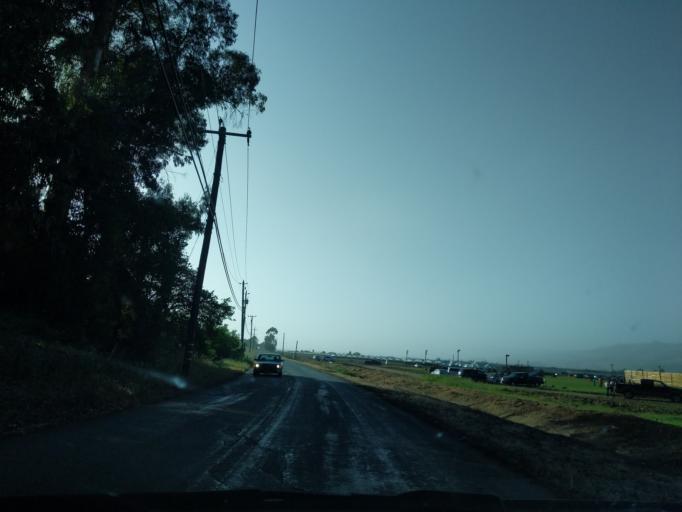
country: US
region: California
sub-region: San Benito County
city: Aromas
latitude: 36.8842
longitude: -121.6818
